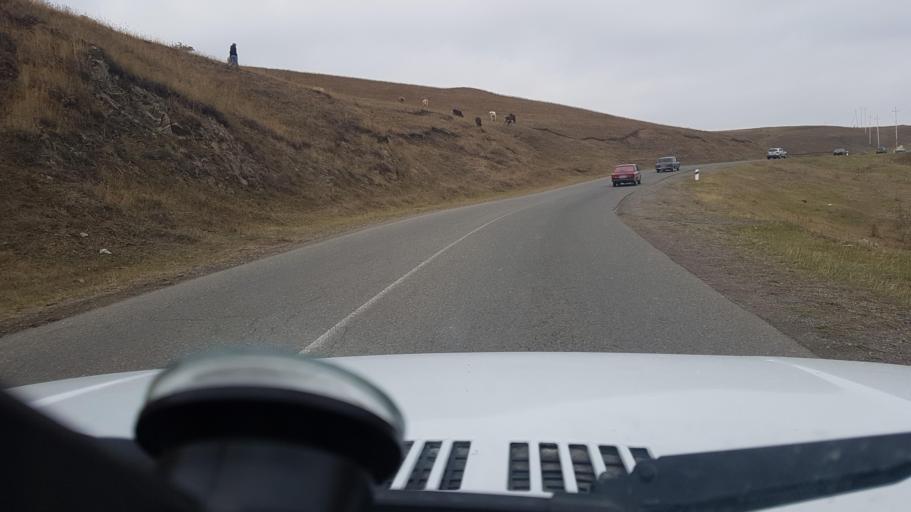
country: AZ
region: Gadabay Rayon
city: Ariqdam
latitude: 40.6163
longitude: 45.8103
